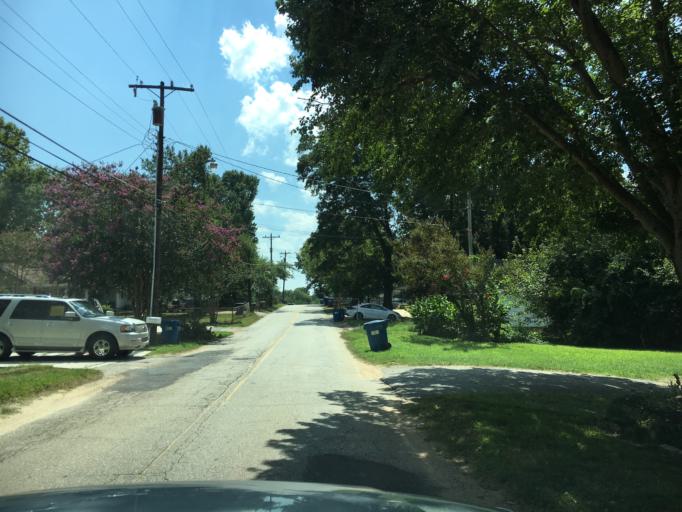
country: US
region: South Carolina
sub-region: Spartanburg County
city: Duncan
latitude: 34.9330
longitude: -82.1345
